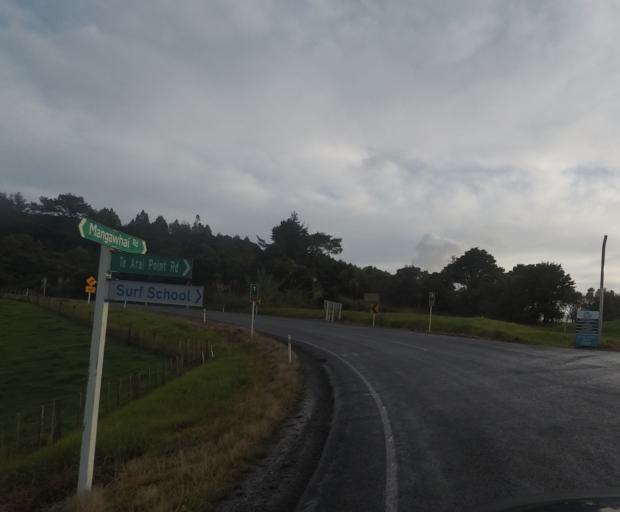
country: NZ
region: Auckland
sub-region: Auckland
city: Wellsford
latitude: -36.1691
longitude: 174.5816
